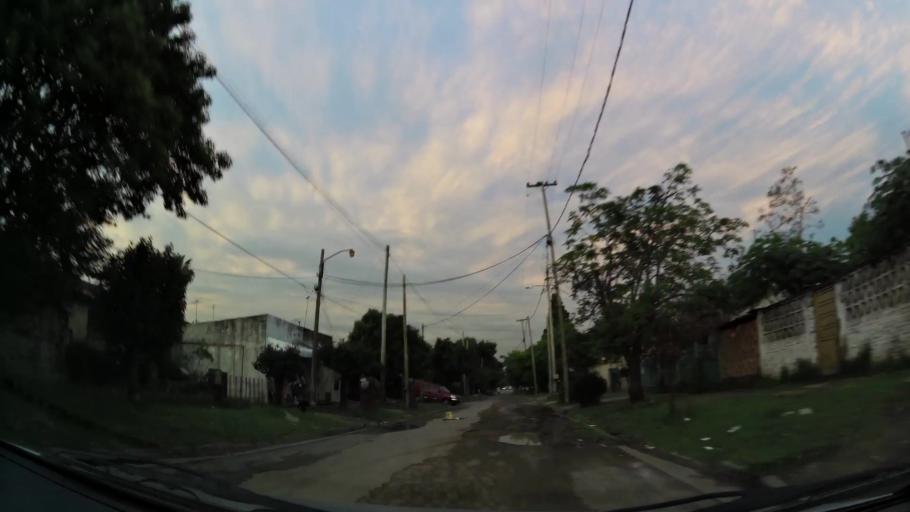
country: AR
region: Buenos Aires
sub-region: Partido de Lomas de Zamora
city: Lomas de Zamora
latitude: -34.7556
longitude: -58.3640
